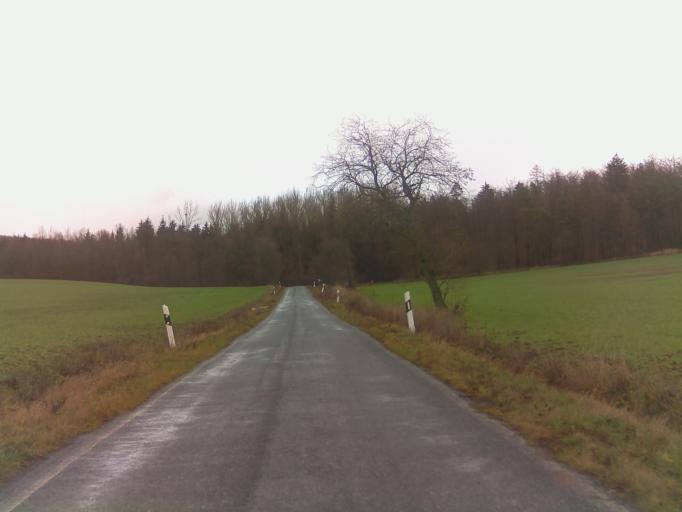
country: DE
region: Bavaria
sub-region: Regierungsbezirk Unterfranken
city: Willmars
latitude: 50.5360
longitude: 10.2310
